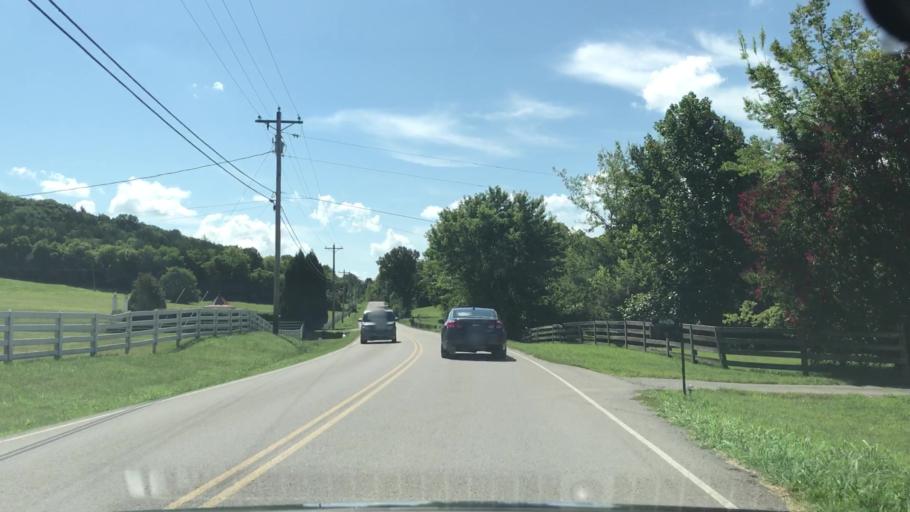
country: US
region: Tennessee
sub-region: Williamson County
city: Franklin
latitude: 35.9588
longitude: -86.8519
